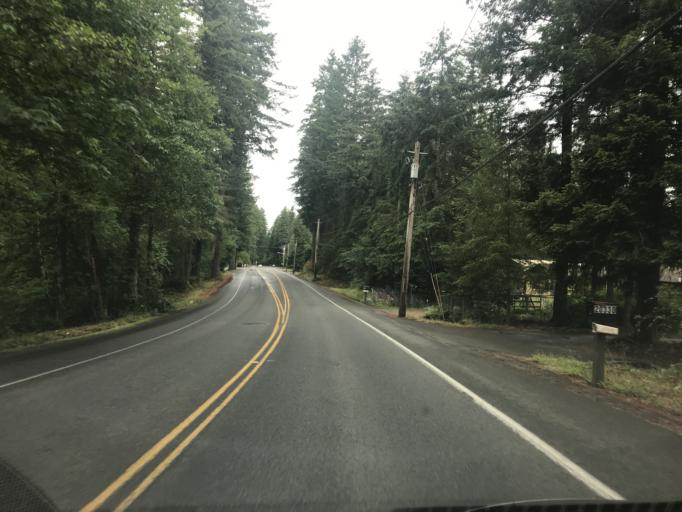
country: US
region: Washington
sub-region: King County
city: Lake Morton-Berrydale
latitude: 47.3427
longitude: -122.0702
